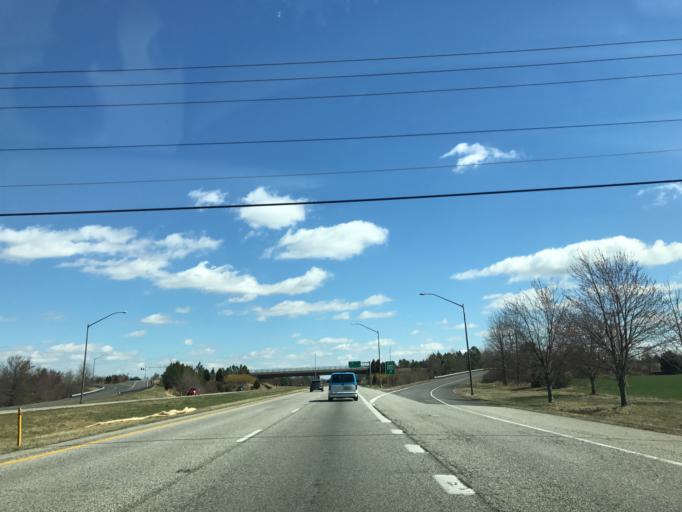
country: US
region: Maryland
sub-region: Queen Anne's County
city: Centreville
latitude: 39.0144
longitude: -76.0800
